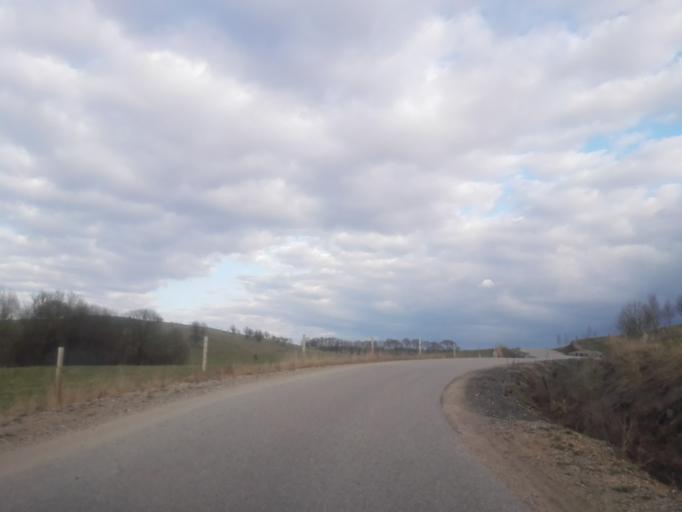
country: PL
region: Podlasie
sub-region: Suwalki
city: Suwalki
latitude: 54.2039
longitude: 22.9838
